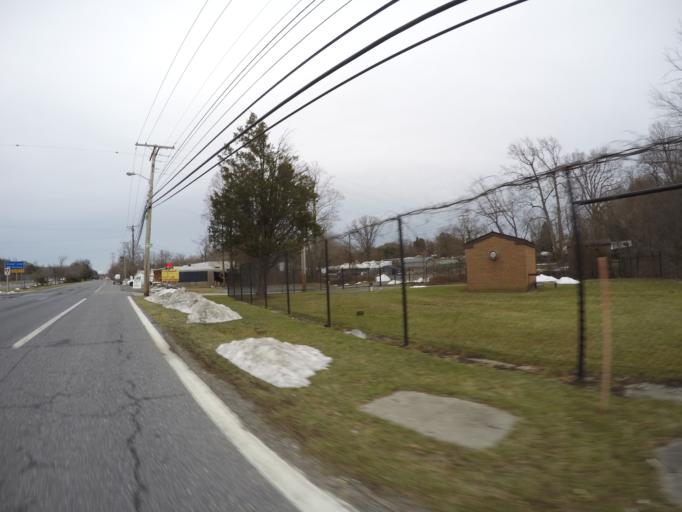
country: US
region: Maryland
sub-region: Anne Arundel County
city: Ferndale
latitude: 39.1635
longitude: -76.6542
